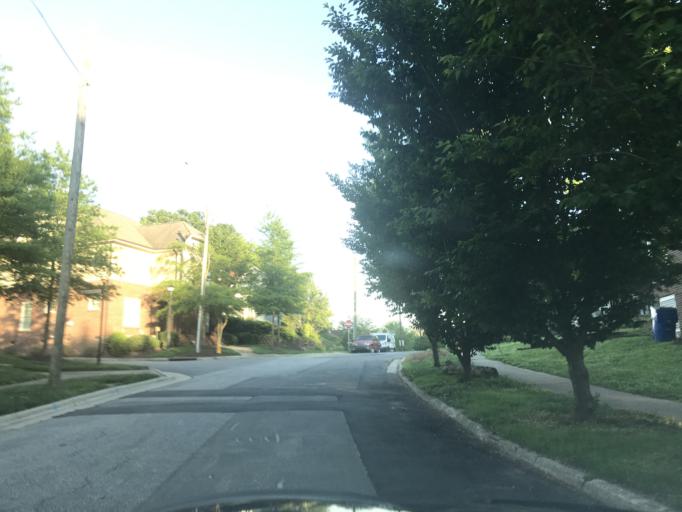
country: US
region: North Carolina
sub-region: Wake County
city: Raleigh
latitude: 35.8000
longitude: -78.6276
